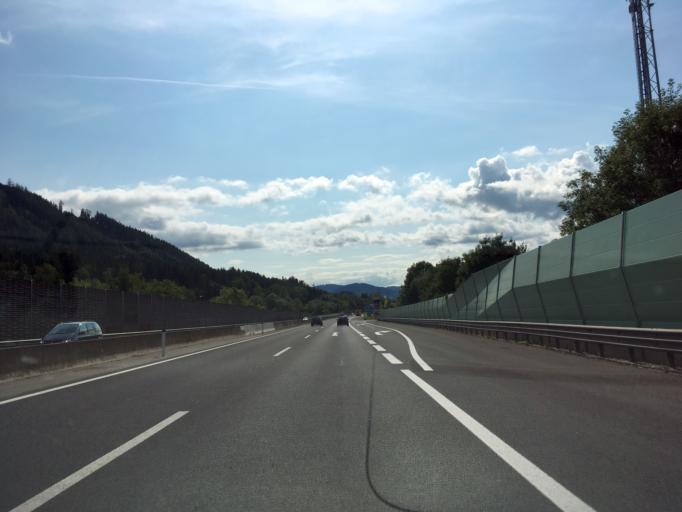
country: AT
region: Styria
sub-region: Politischer Bezirk Bruck-Muerzzuschlag
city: Sankt Marein im Muerztal
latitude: 47.4680
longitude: 15.3756
